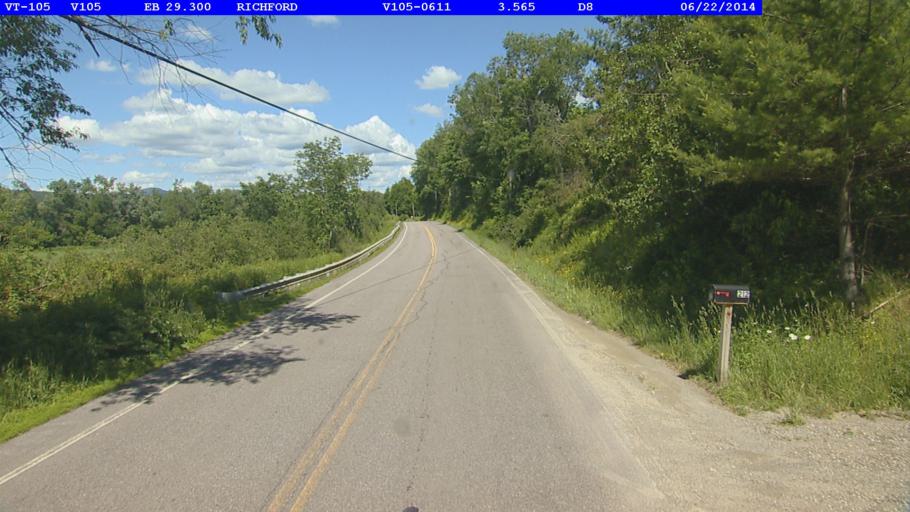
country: US
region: Vermont
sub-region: Franklin County
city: Richford
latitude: 44.9886
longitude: -72.6474
